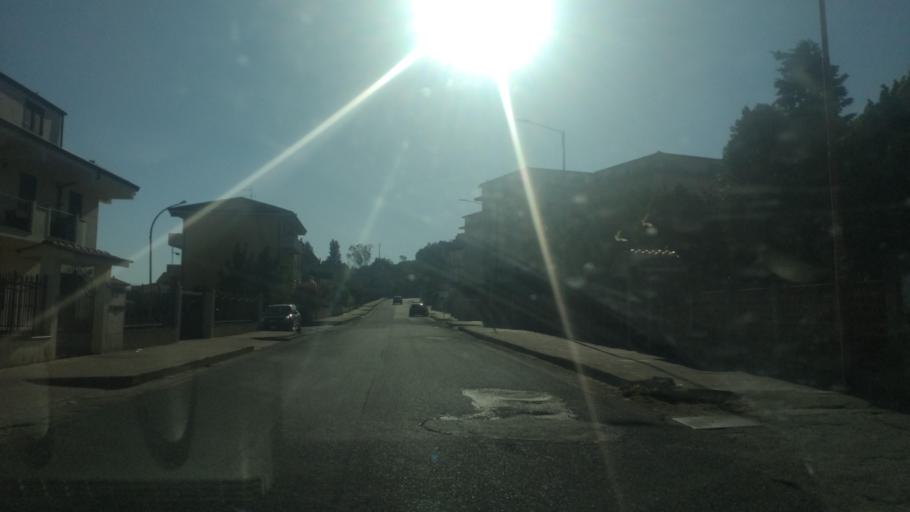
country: IT
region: Calabria
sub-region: Provincia di Catanzaro
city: Squillace
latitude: 38.7804
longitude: 16.5101
